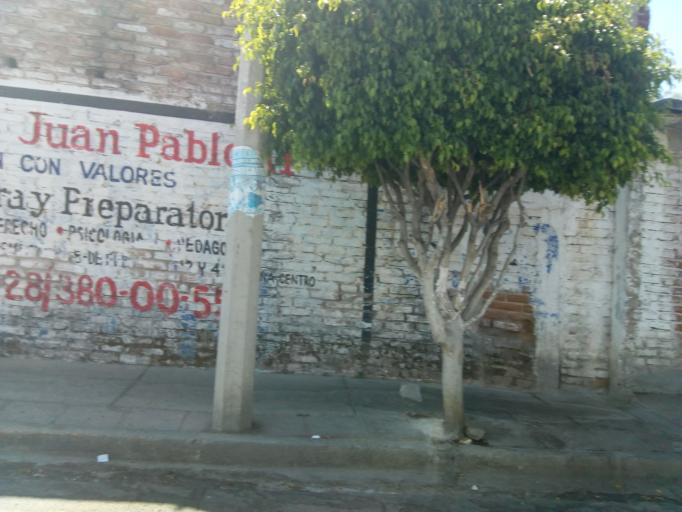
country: MX
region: Guanajuato
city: Leon
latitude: 21.1124
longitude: -101.6935
